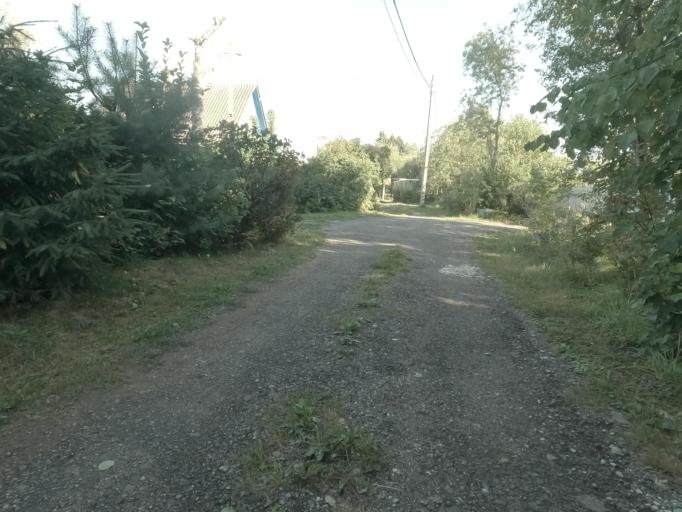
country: RU
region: Leningrad
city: Kirovsk
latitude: 59.9284
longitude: 30.9821
